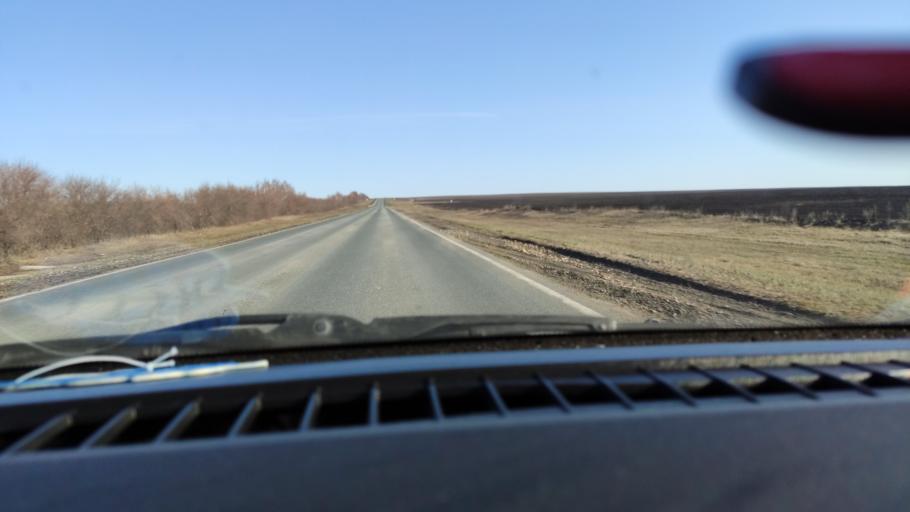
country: RU
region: Saratov
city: Dukhovnitskoye
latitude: 52.7780
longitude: 48.2347
